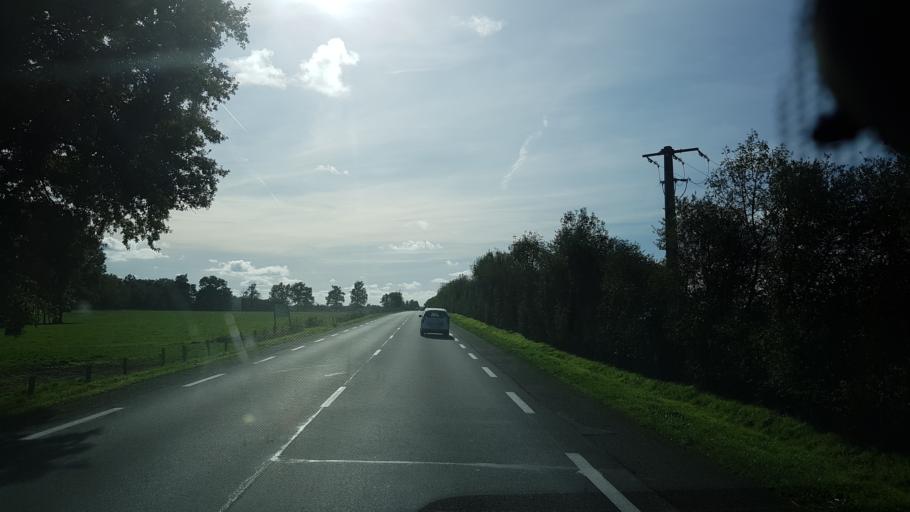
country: FR
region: Poitou-Charentes
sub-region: Departement de la Charente
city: Loubert
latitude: 45.9793
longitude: 0.5992
